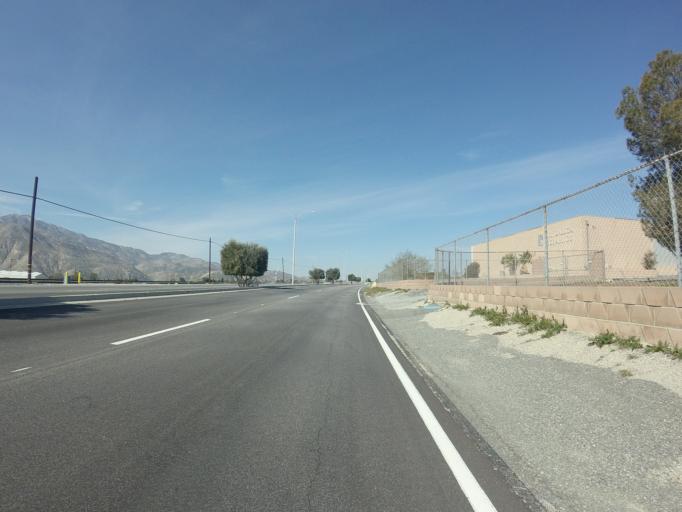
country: US
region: California
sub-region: Riverside County
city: Cabazon
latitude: 33.9161
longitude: -116.7892
